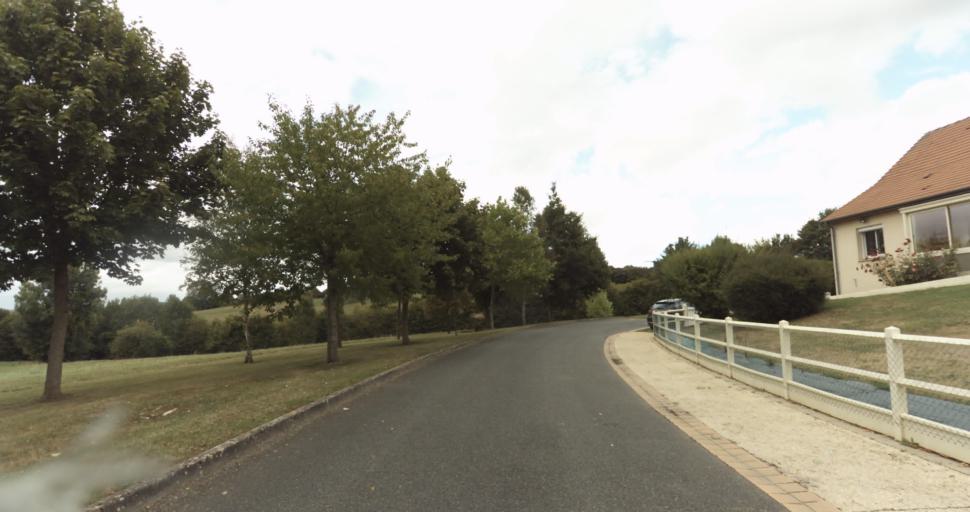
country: FR
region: Lower Normandy
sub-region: Departement de l'Orne
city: Gace
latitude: 48.7883
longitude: 0.3015
